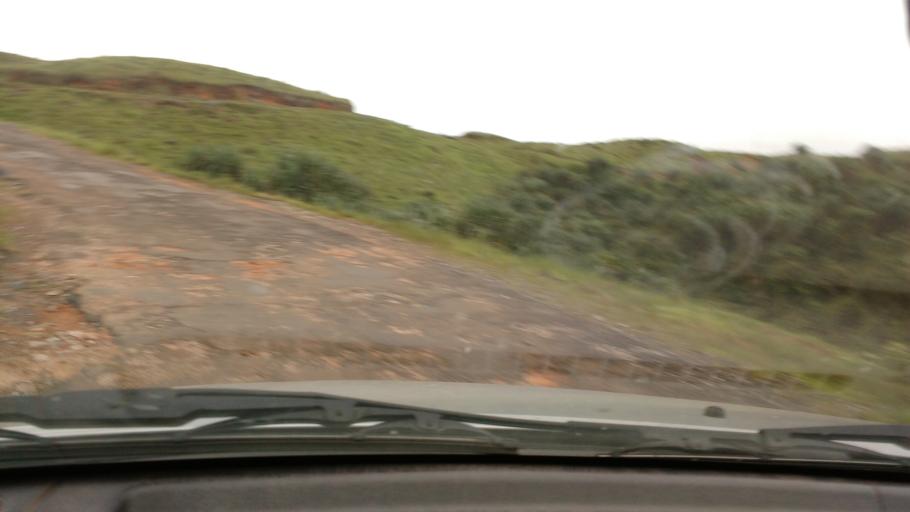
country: IN
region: Meghalaya
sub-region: East Khasi Hills
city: Cherrapunji
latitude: 25.2800
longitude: 91.6981
